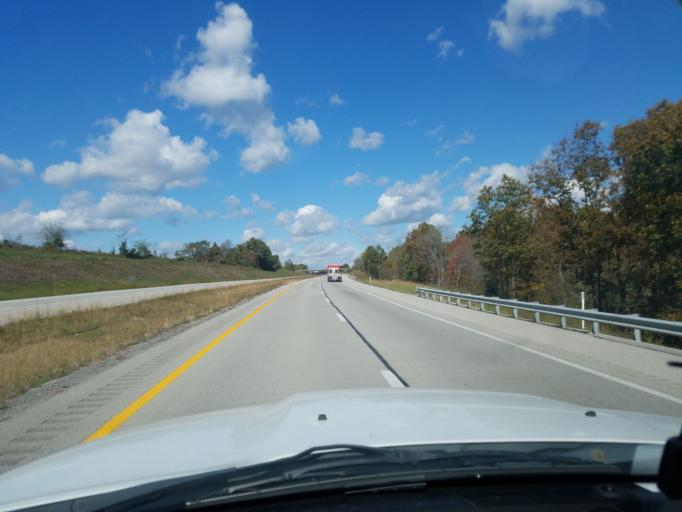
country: US
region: Kentucky
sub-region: Ohio County
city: Hartford
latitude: 37.4853
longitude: -86.9080
